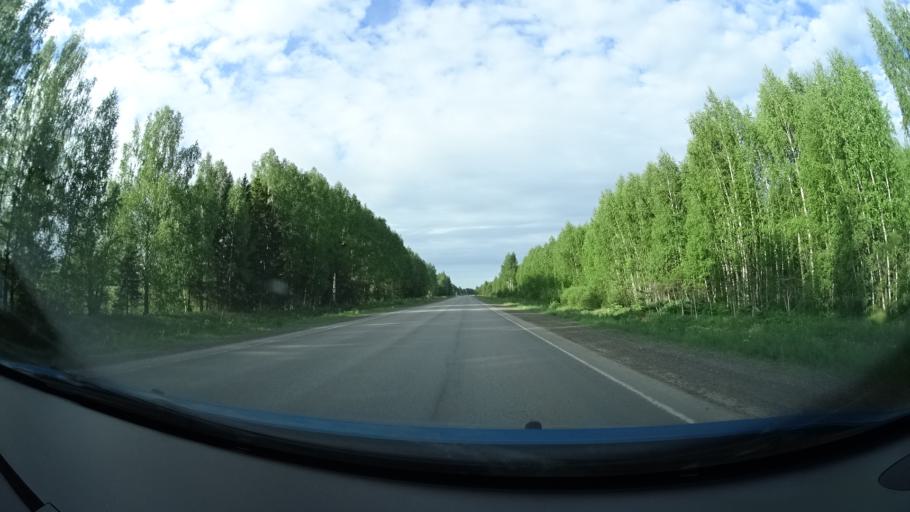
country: RU
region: Perm
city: Osa
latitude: 57.3628
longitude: 55.6028
